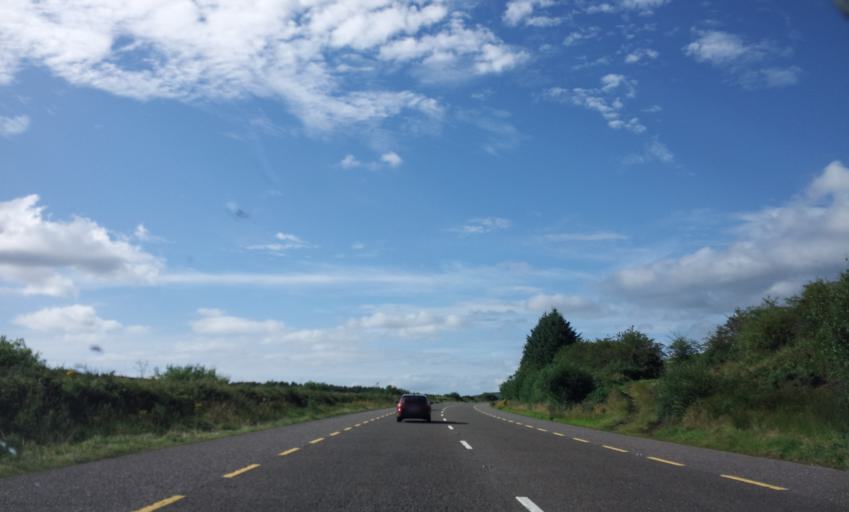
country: IE
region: Munster
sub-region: County Cork
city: Millstreet
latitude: 51.9639
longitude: -9.2459
